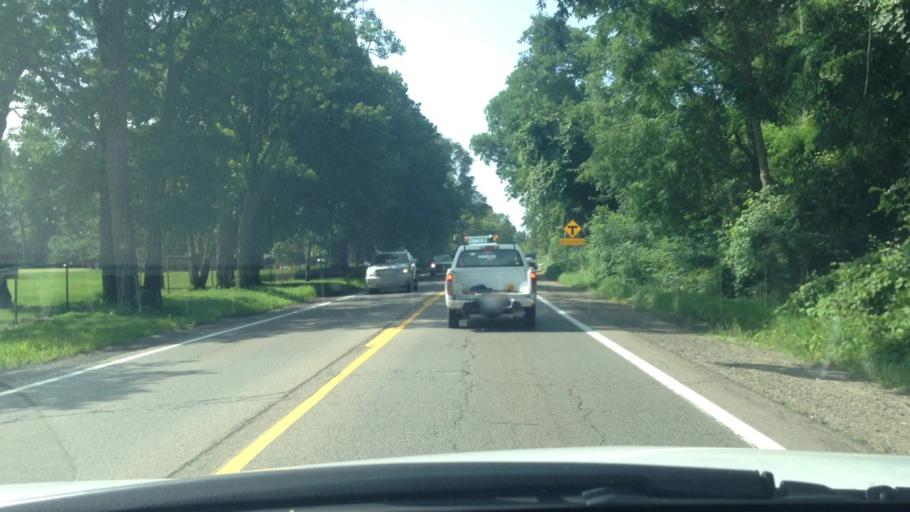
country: US
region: Michigan
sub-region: Oakland County
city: Wolverine Lake
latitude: 42.5801
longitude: -83.4464
